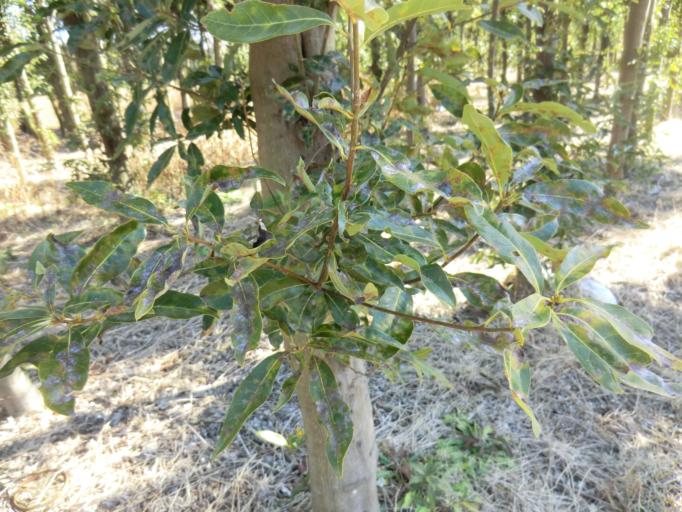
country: JP
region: Ibaraki
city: Naka
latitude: 36.0478
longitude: 140.1393
